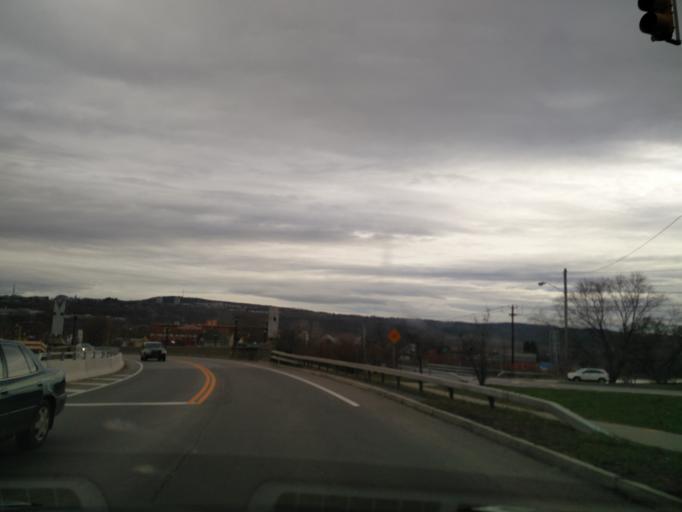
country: US
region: New York
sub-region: Tompkins County
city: Ithaca
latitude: 42.4416
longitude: -76.5153
